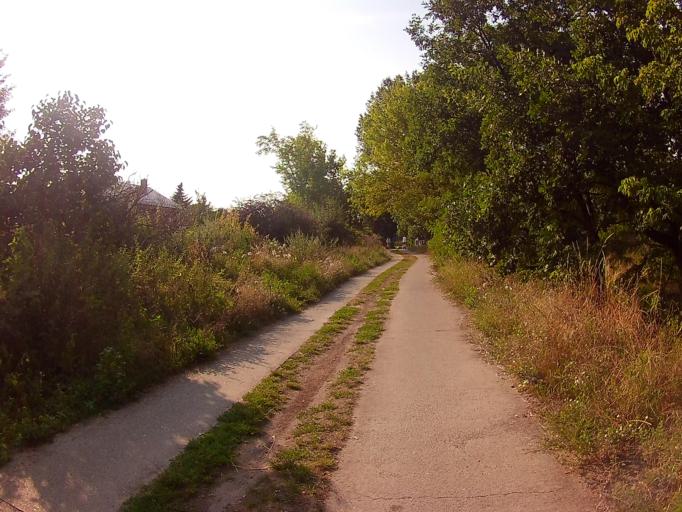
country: DE
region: Berlin
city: Biesdorf
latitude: 52.4780
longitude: 13.5648
